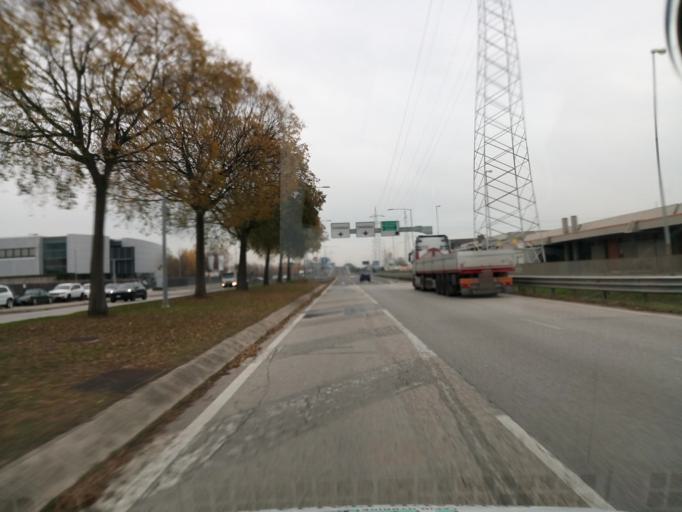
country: IT
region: Veneto
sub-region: Provincia di Padova
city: Villatora
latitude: 45.3906
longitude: 11.9477
